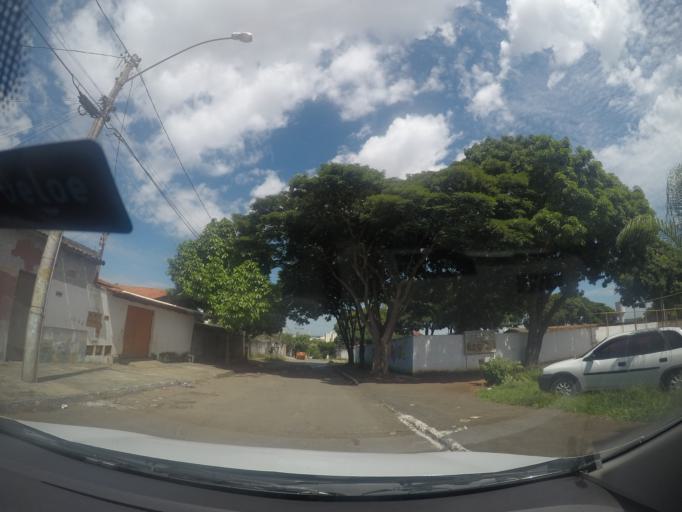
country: BR
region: Goias
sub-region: Goiania
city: Goiania
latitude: -16.7008
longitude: -49.3159
